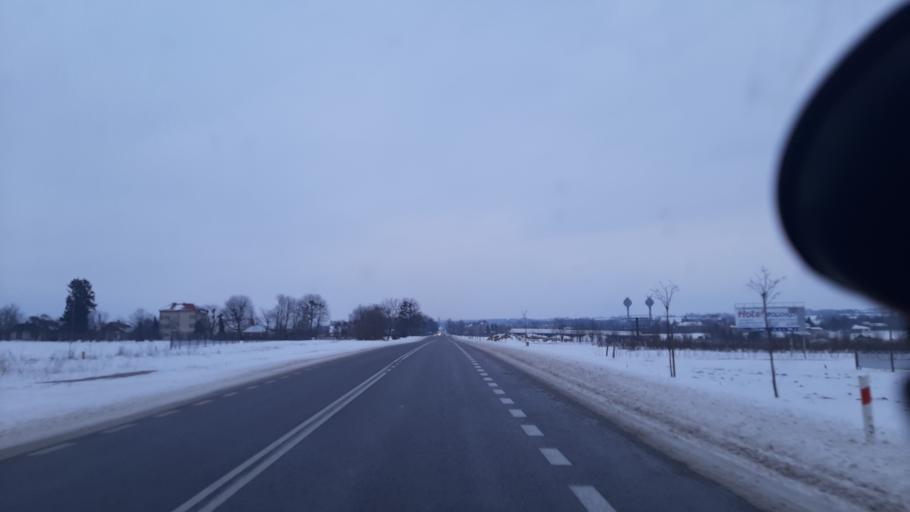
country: PL
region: Lublin Voivodeship
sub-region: Powiat pulawski
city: Markuszow
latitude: 51.3681
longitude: 22.2851
